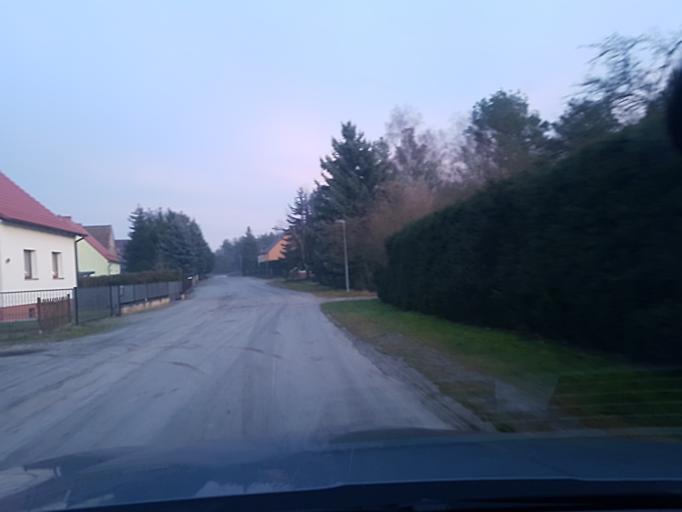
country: DE
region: Brandenburg
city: Doberlug-Kirchhain
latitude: 51.6257
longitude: 13.5849
